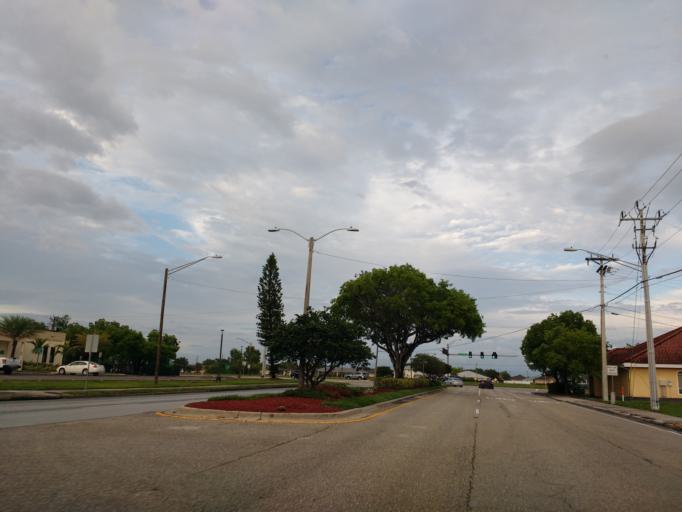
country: US
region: Florida
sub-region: Lee County
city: Lochmoor Waterway Estates
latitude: 26.6297
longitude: -81.9575
